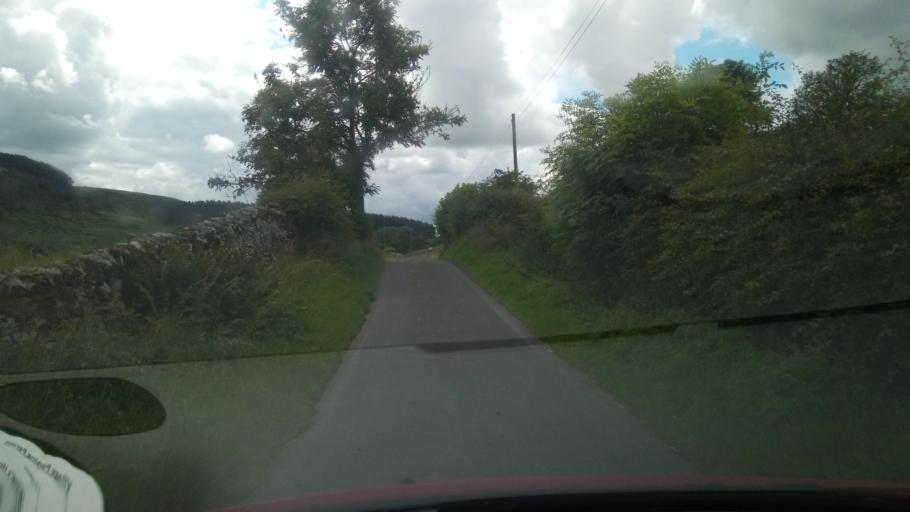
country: GB
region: Scotland
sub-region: The Scottish Borders
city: Hawick
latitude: 55.4157
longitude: -2.7569
